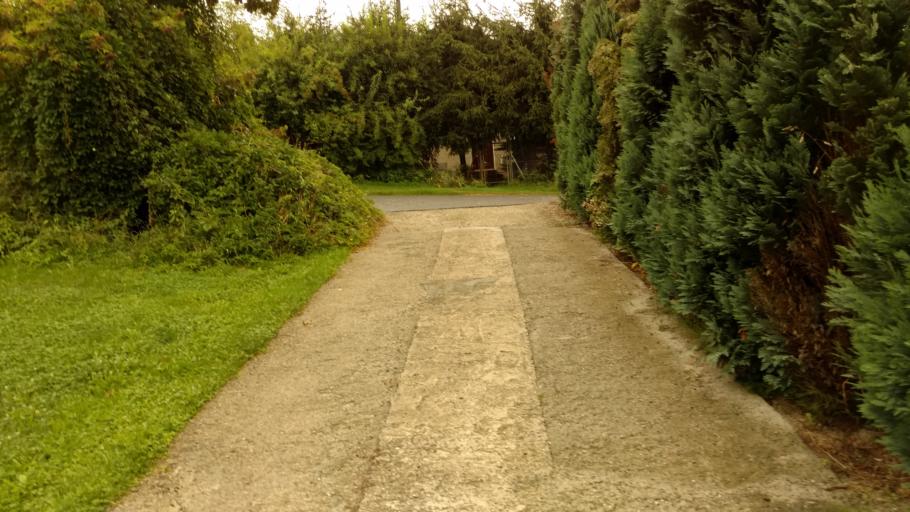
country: PL
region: Lesser Poland Voivodeship
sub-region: Powiat krakowski
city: Michalowice
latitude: 50.1332
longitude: 19.9696
